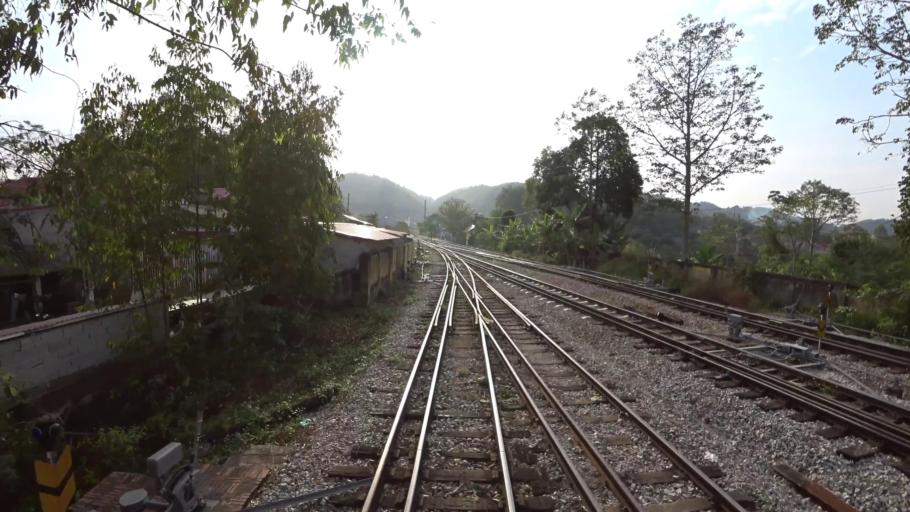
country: VN
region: Lang Son
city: Thi Tran Cao Loc
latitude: 21.9397
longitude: 106.6942
